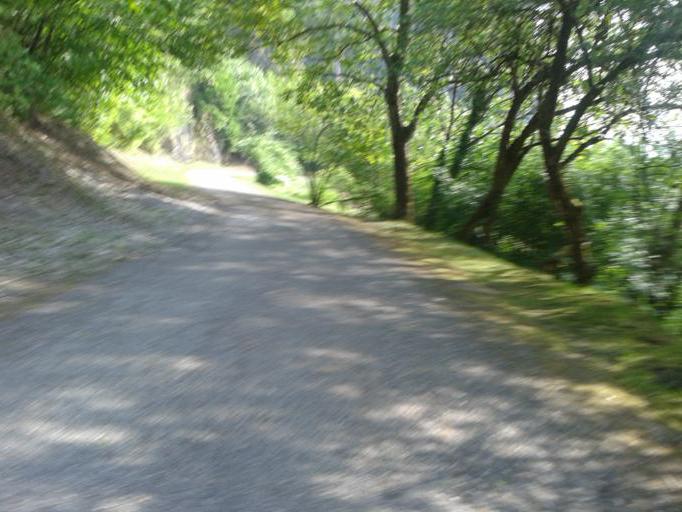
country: IT
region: Trentino-Alto Adige
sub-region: Provincia di Trento
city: Storo
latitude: 45.8619
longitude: 10.5793
